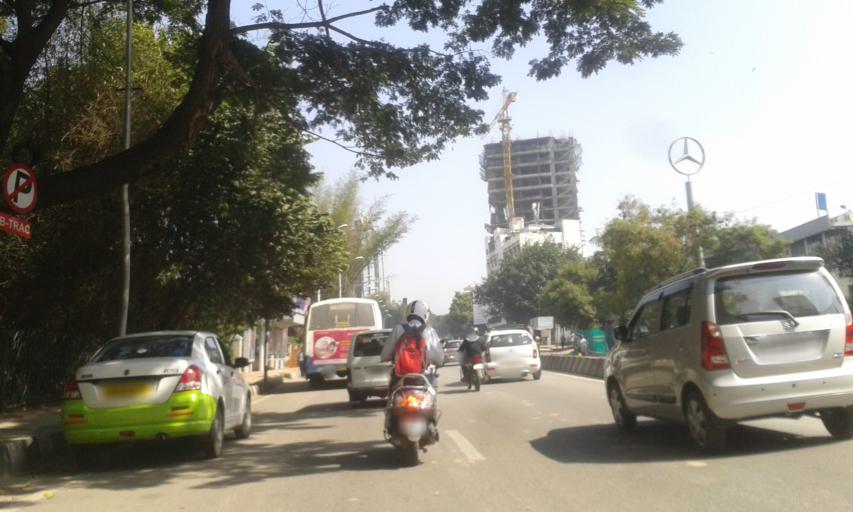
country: IN
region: Karnataka
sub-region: Bangalore Urban
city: Bangalore
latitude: 12.9734
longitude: 77.5951
